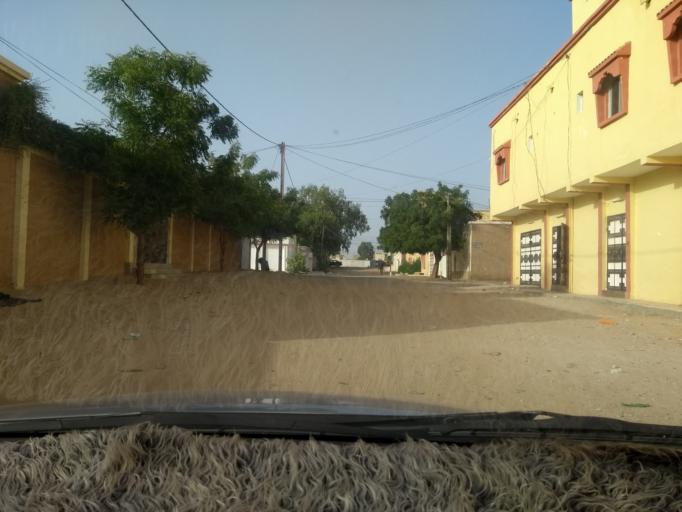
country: MR
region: Nouakchott
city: Nouakchott
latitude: 18.1087
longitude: -15.9741
